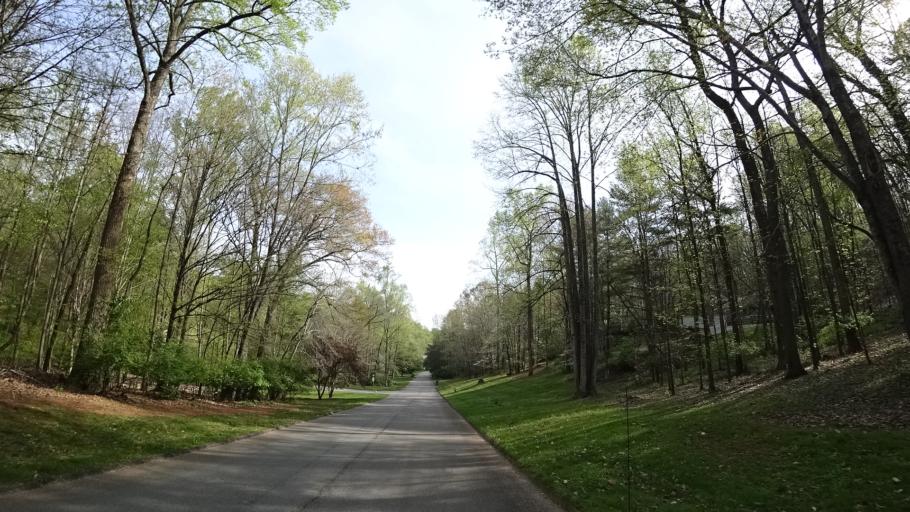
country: US
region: Tennessee
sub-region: Knox County
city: Knoxville
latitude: 35.9026
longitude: -83.9884
